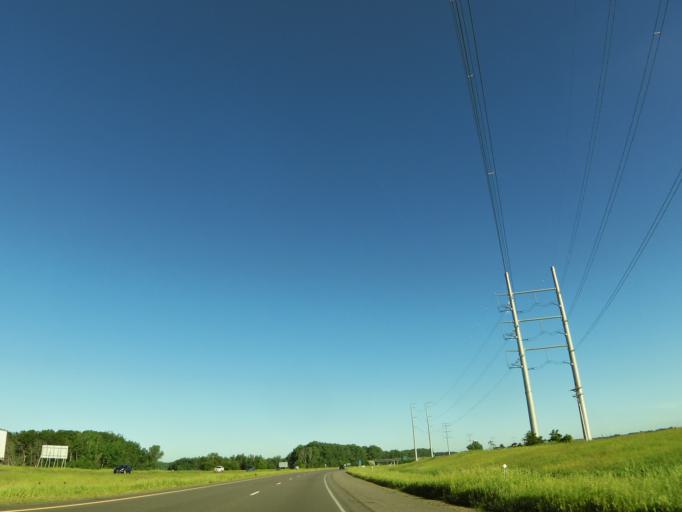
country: US
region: Minnesota
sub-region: Stearns County
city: Waite Park
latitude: 45.4988
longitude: -94.2596
